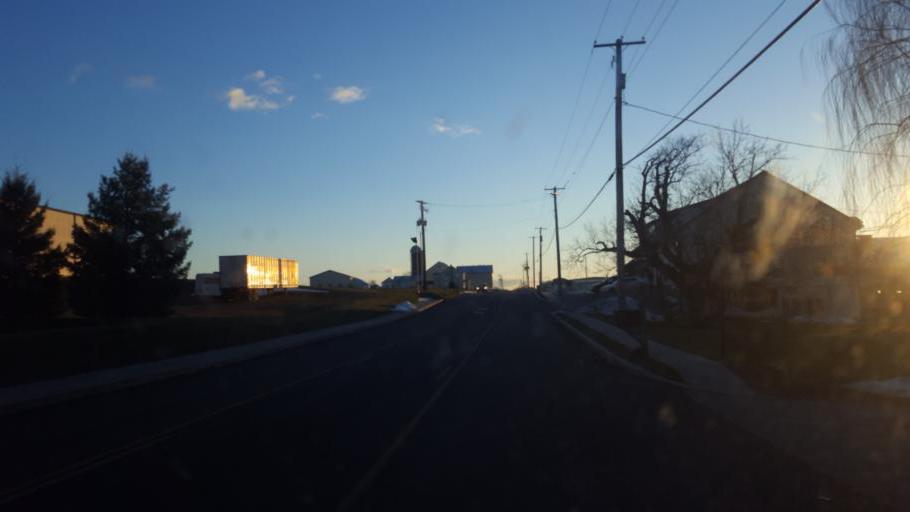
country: US
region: Pennsylvania
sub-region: Lancaster County
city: New Holland
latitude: 40.0907
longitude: -76.0965
